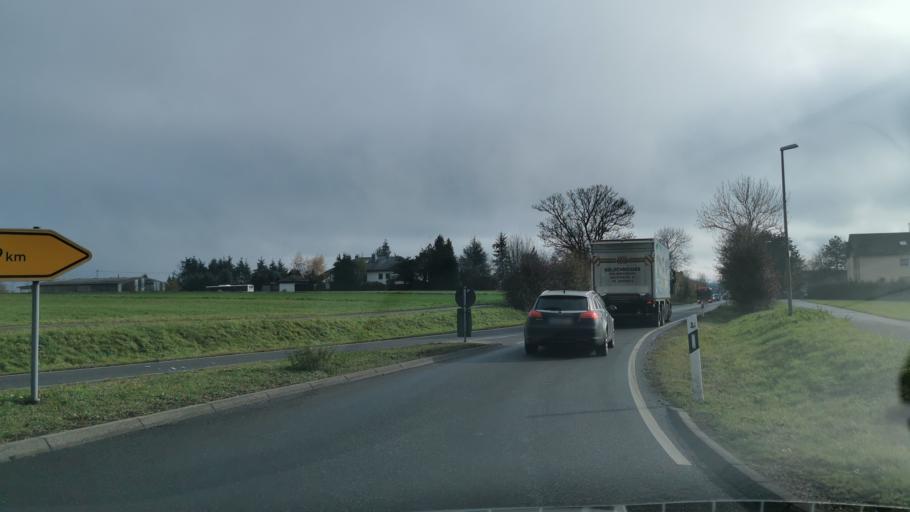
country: DE
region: Rheinland-Pfalz
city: Faid
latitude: 50.1490
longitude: 7.1181
